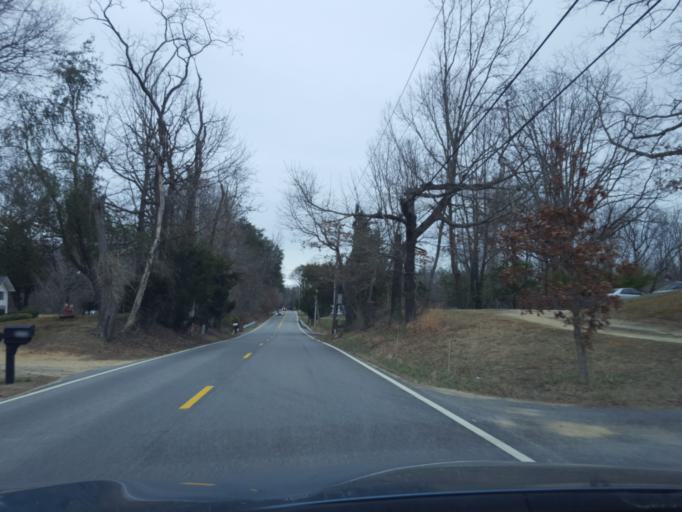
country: US
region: Maryland
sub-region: Calvert County
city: Prince Frederick
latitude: 38.4986
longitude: -76.5801
